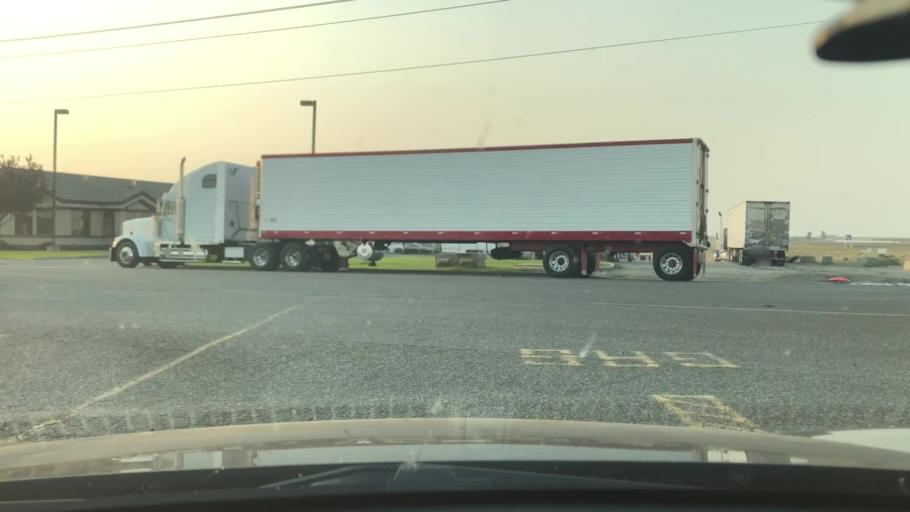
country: US
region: Washington
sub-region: Franklin County
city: Pasco
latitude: 46.2626
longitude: -119.0823
